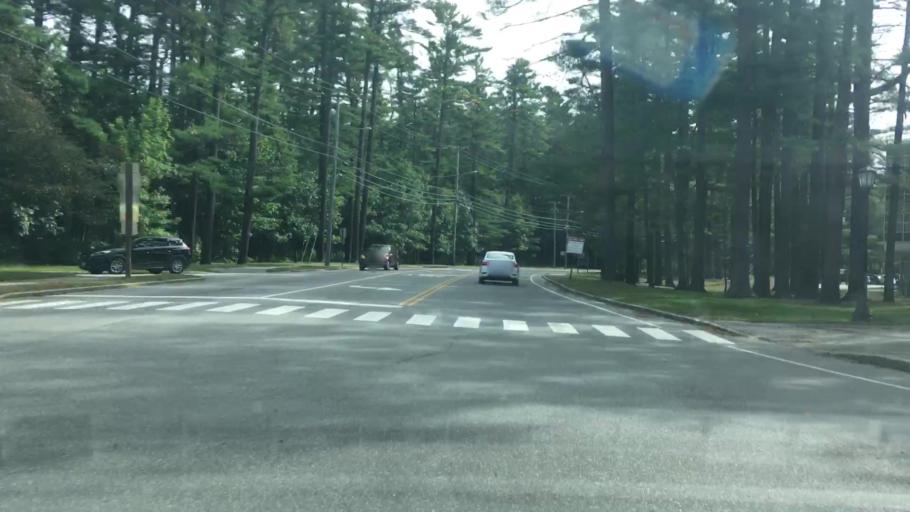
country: US
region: Maine
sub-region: Cumberland County
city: Brunswick
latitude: 43.9101
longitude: -69.9594
